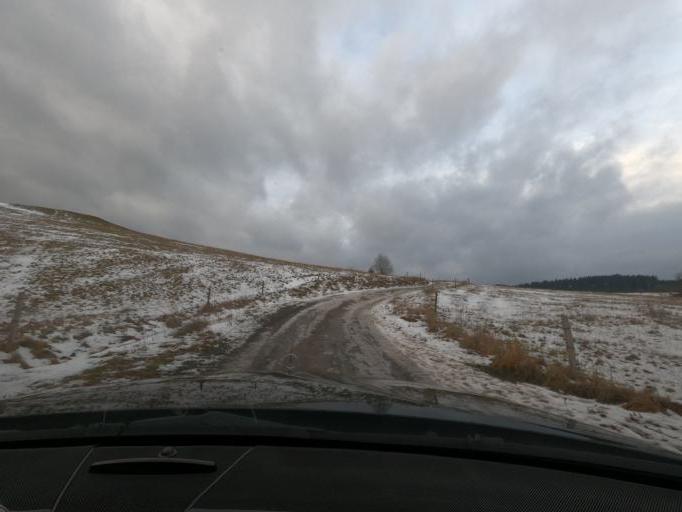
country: DE
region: Thuringia
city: Finsterbergen
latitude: 50.8285
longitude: 10.5926
